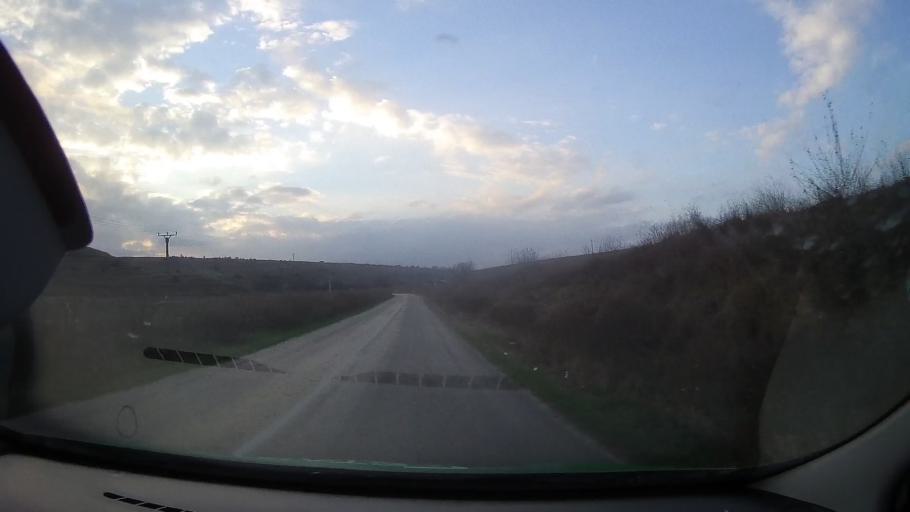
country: RO
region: Constanta
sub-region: Comuna Baneasa
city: Baneasa
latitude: 44.0594
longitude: 27.7135
